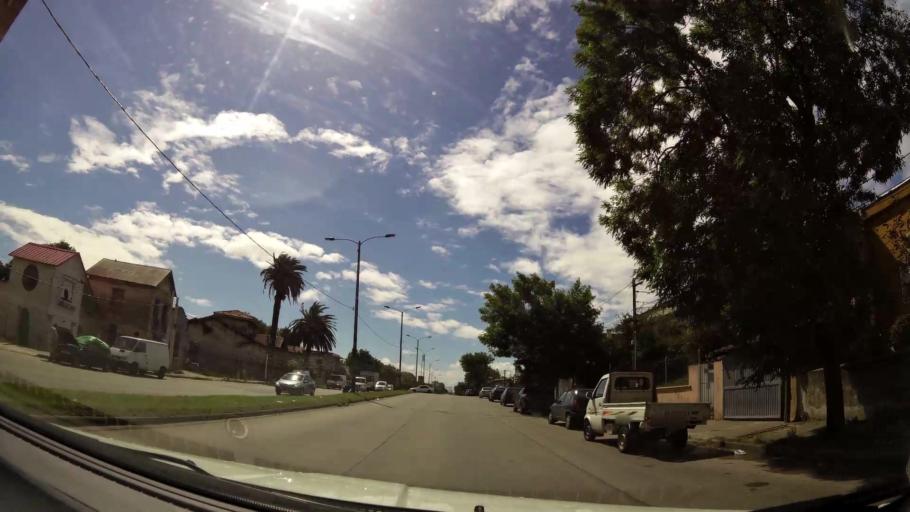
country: UY
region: Montevideo
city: Montevideo
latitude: -34.8592
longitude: -56.1741
